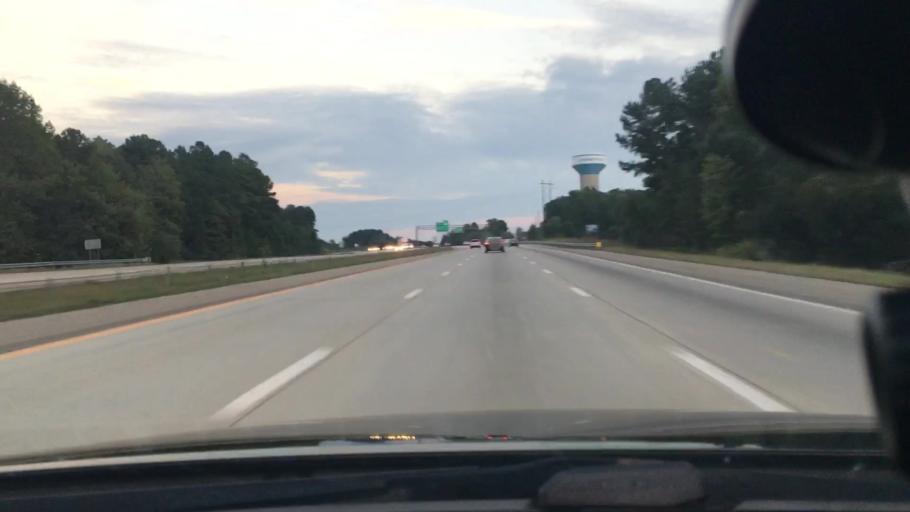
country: US
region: North Carolina
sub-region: Wake County
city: Knightdale
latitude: 35.7709
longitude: -78.5310
